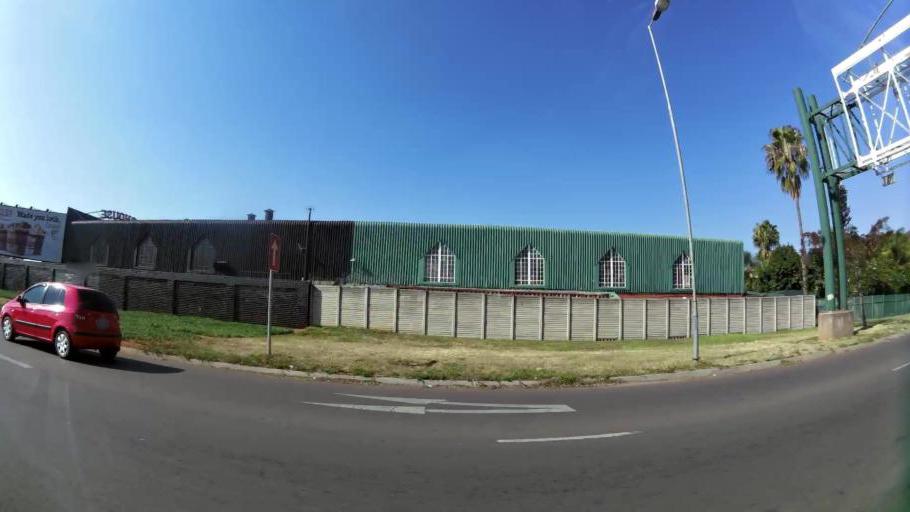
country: ZA
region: Gauteng
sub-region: City of Tshwane Metropolitan Municipality
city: Pretoria
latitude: -25.6843
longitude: 28.1913
